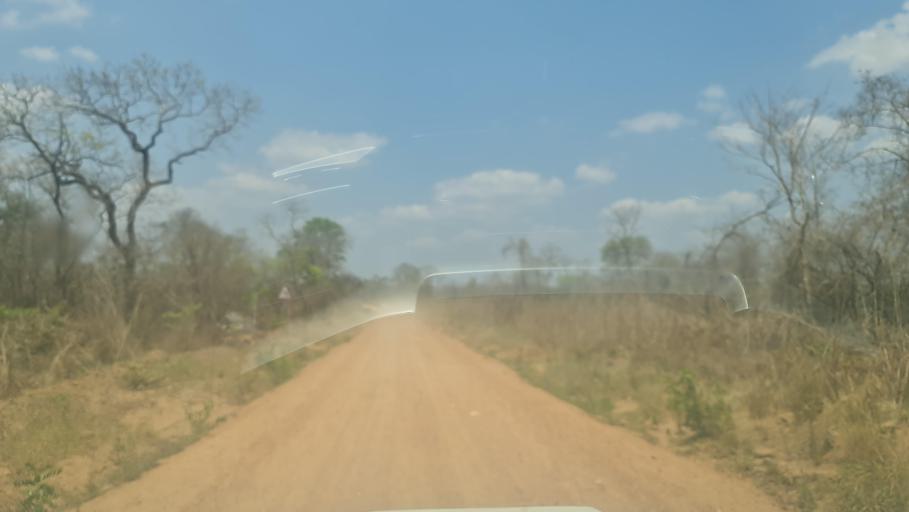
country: MW
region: Southern Region
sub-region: Nsanje District
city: Nsanje
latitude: -17.5659
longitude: 35.9023
